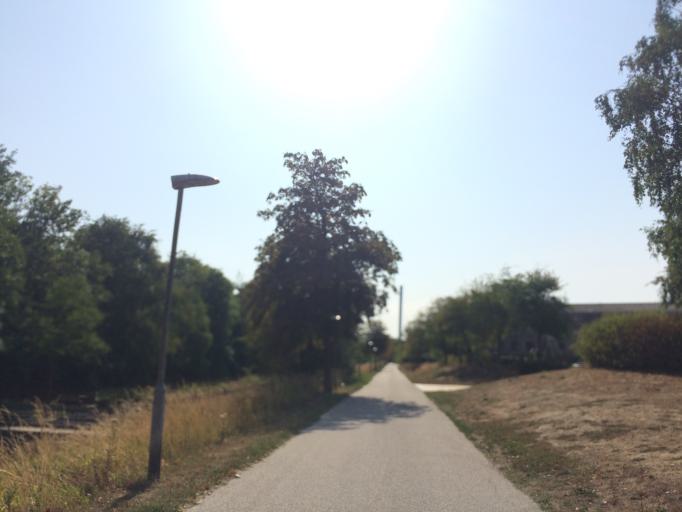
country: DK
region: Capital Region
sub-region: Hvidovre Kommune
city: Hvidovre
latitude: 55.6254
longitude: 12.4520
